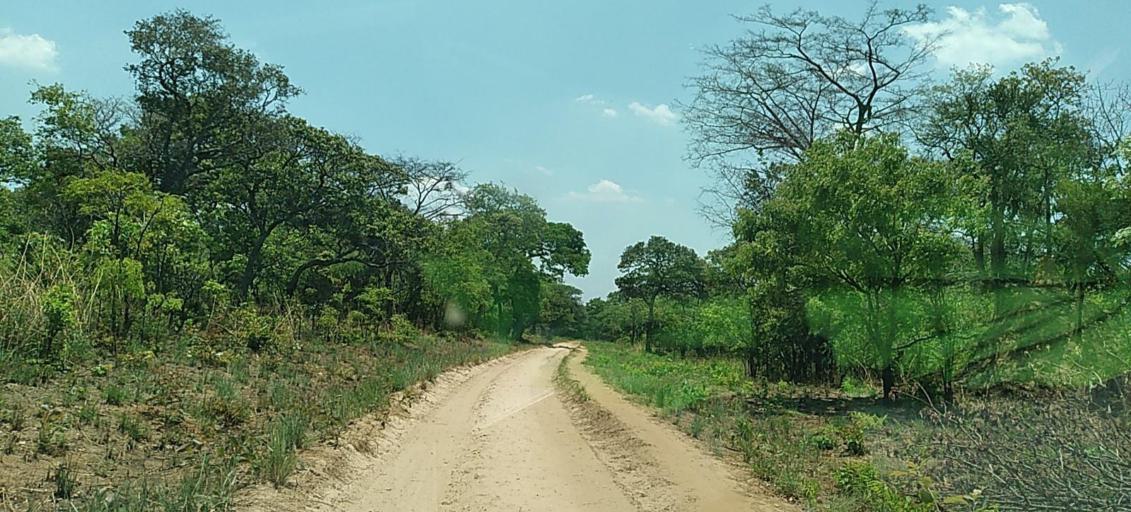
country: CD
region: Katanga
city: Kolwezi
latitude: -11.3648
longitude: 25.2075
